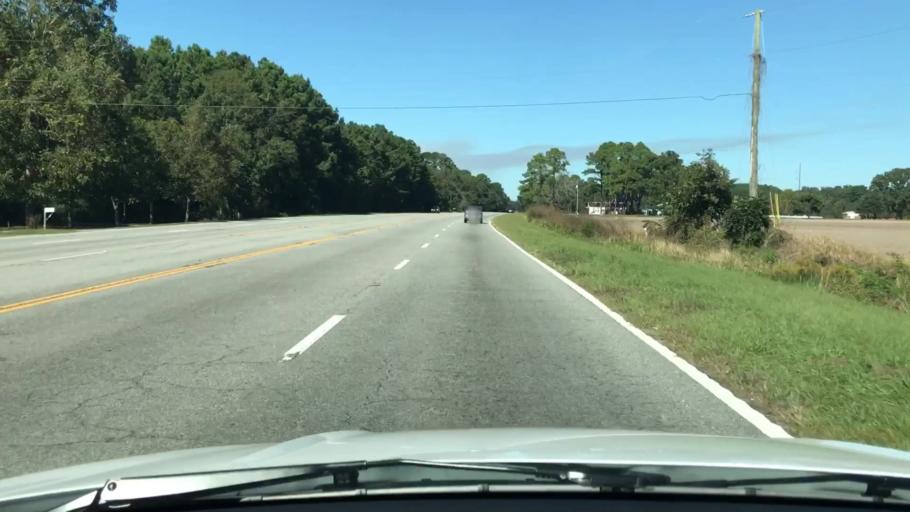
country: US
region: South Carolina
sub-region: Beaufort County
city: Laurel Bay
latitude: 32.5479
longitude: -80.7440
